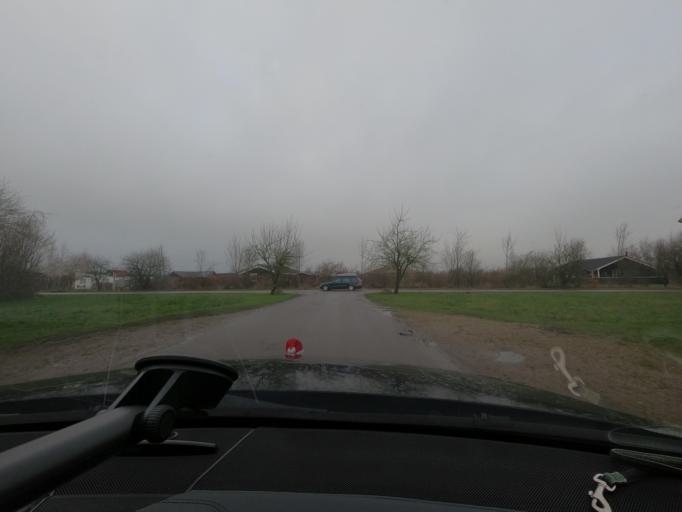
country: DK
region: South Denmark
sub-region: Sonderborg Kommune
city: Horuphav
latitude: 54.8776
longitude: 10.0138
